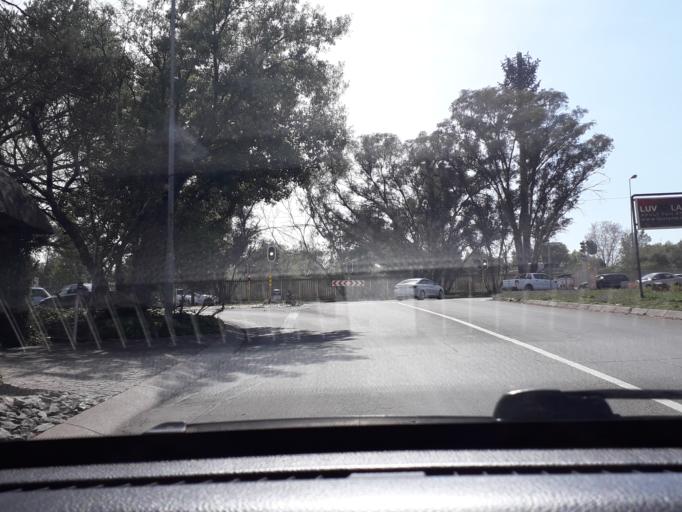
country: ZA
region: Gauteng
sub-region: City of Johannesburg Metropolitan Municipality
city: Midrand
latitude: -26.0480
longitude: 28.0707
